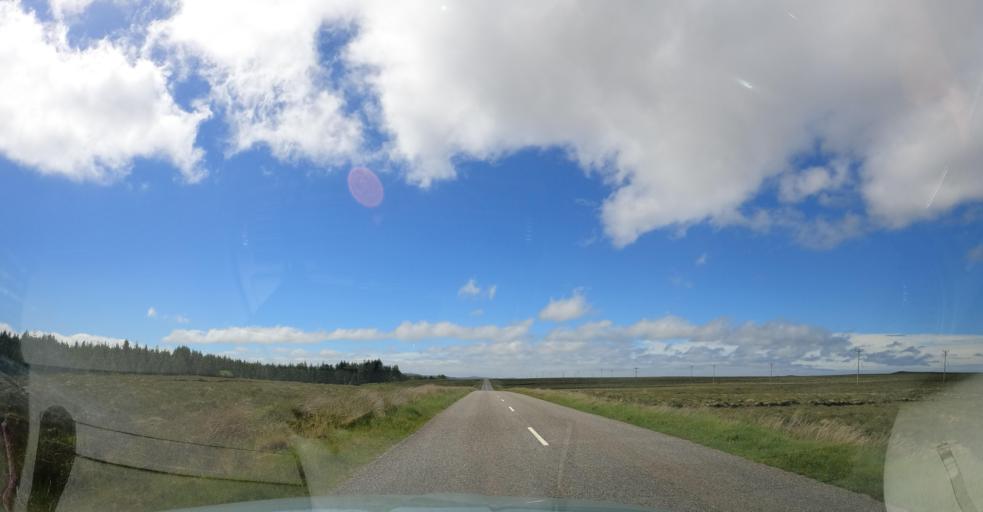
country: GB
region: Scotland
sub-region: Eilean Siar
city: Isle of Lewis
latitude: 58.1793
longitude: -6.6458
